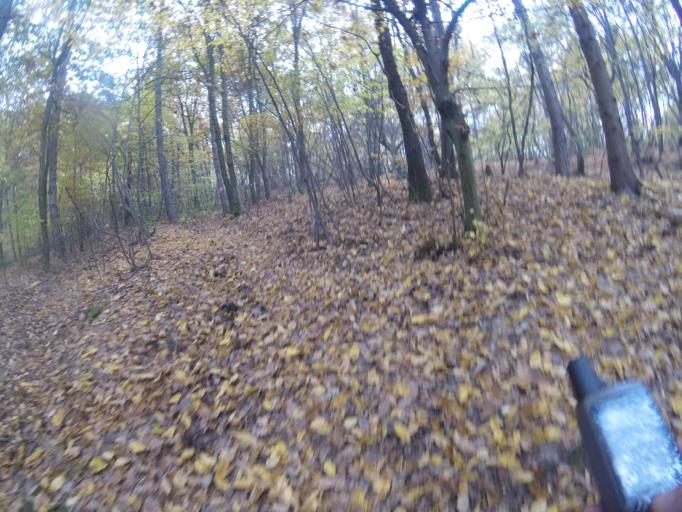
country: HU
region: Borsod-Abauj-Zemplen
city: Gonc
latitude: 48.4632
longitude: 21.2977
